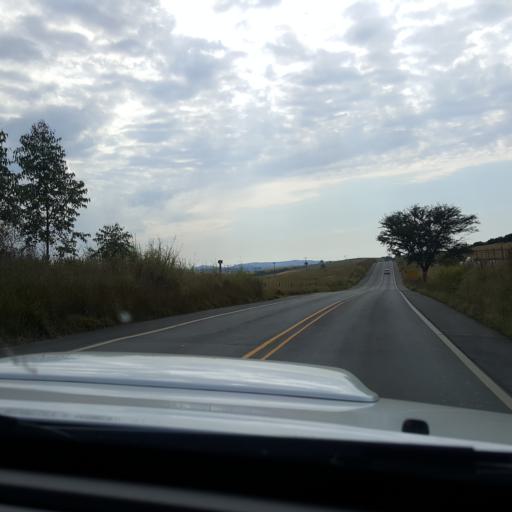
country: BR
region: Sao Paulo
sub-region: Itaporanga
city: Itaporanga
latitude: -23.7664
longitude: -49.4467
